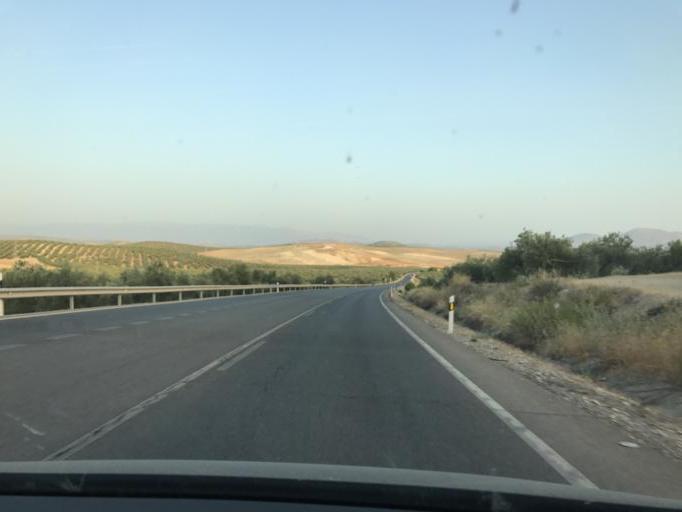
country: ES
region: Andalusia
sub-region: Provincia de Jaen
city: Ubeda
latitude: 37.9697
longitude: -3.3681
